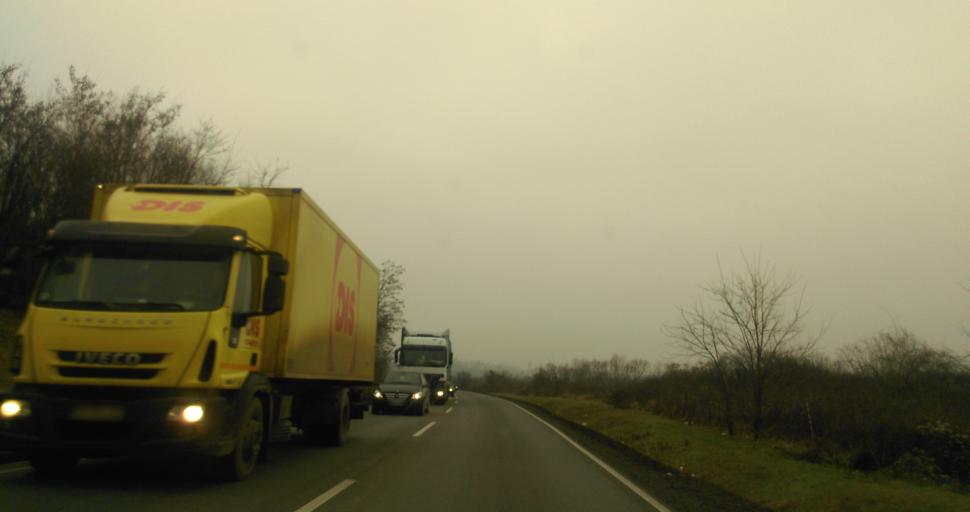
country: RS
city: Rusanj
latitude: 44.7151
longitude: 20.4783
